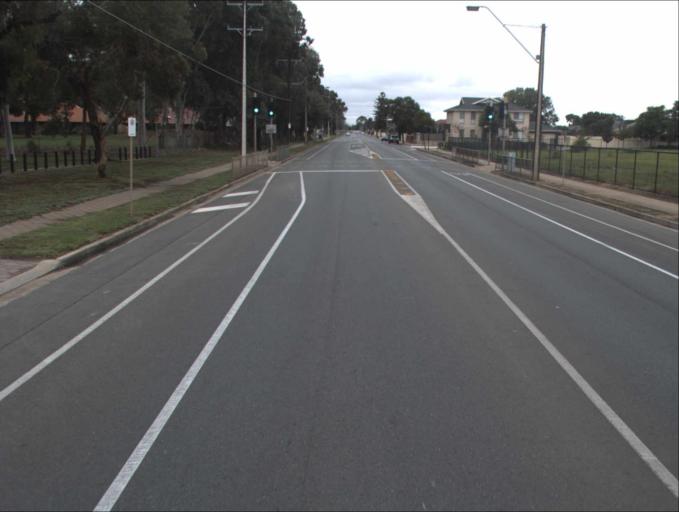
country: AU
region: South Australia
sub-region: Charles Sturt
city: Woodville
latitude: -34.8664
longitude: 138.5657
